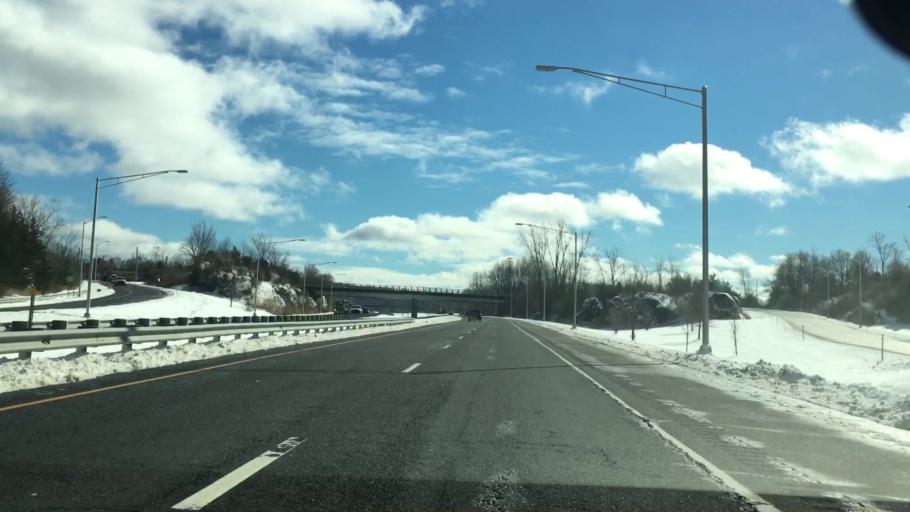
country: US
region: Connecticut
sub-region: Fairfield County
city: Danbury
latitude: 41.4746
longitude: -73.4102
